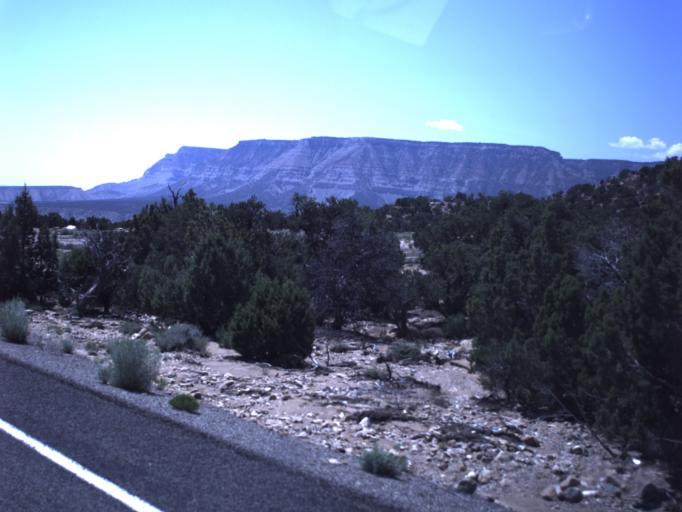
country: US
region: Utah
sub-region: Emery County
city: Orangeville
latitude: 39.3015
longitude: -111.1179
